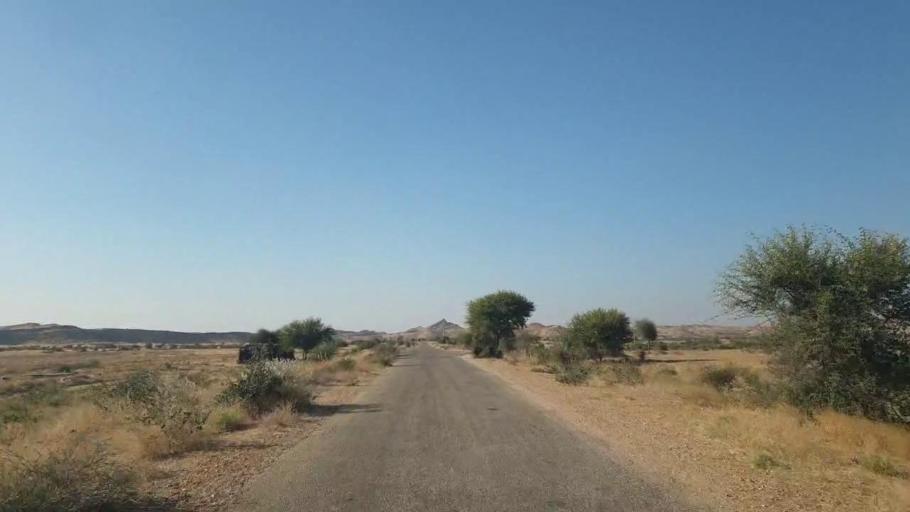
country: PK
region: Sindh
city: Malir Cantonment
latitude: 25.3942
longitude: 67.4975
